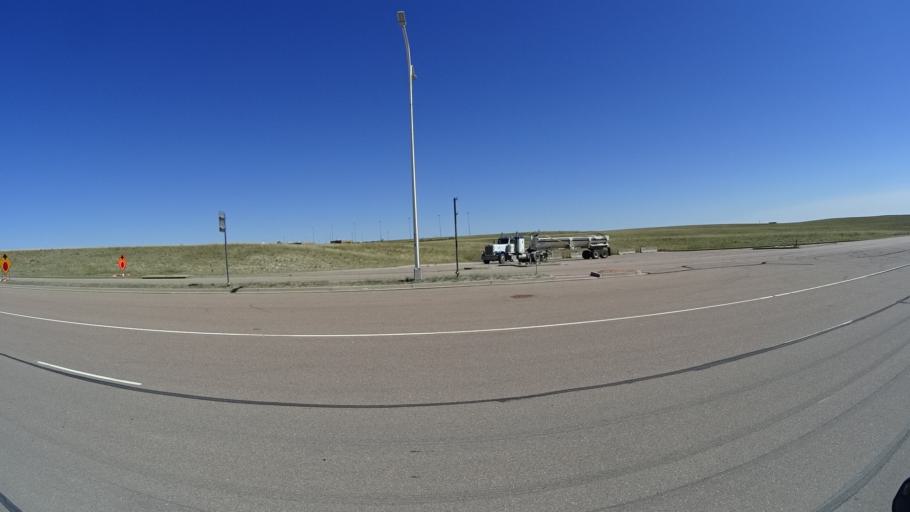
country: US
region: Colorado
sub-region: El Paso County
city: Security-Widefield
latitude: 38.7716
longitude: -104.7005
